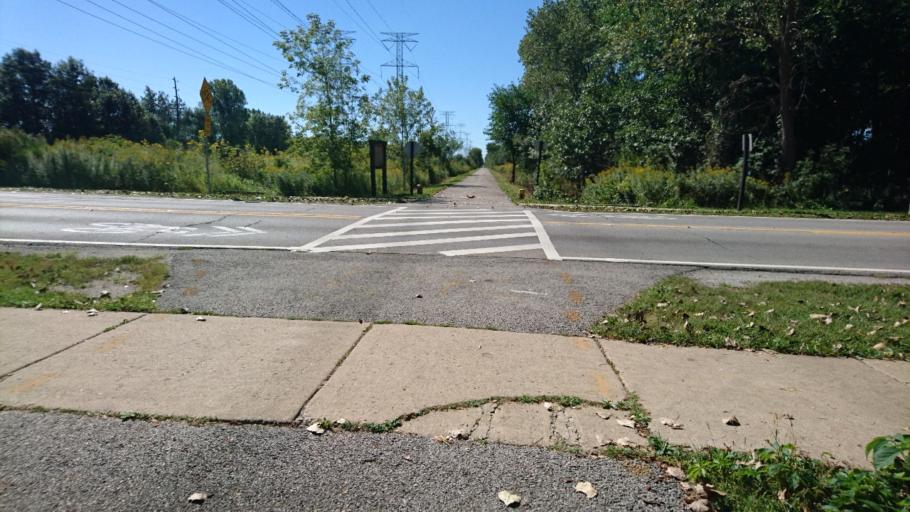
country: US
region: Illinois
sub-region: Cook County
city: Calumet City
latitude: 41.6156
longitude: -87.5494
